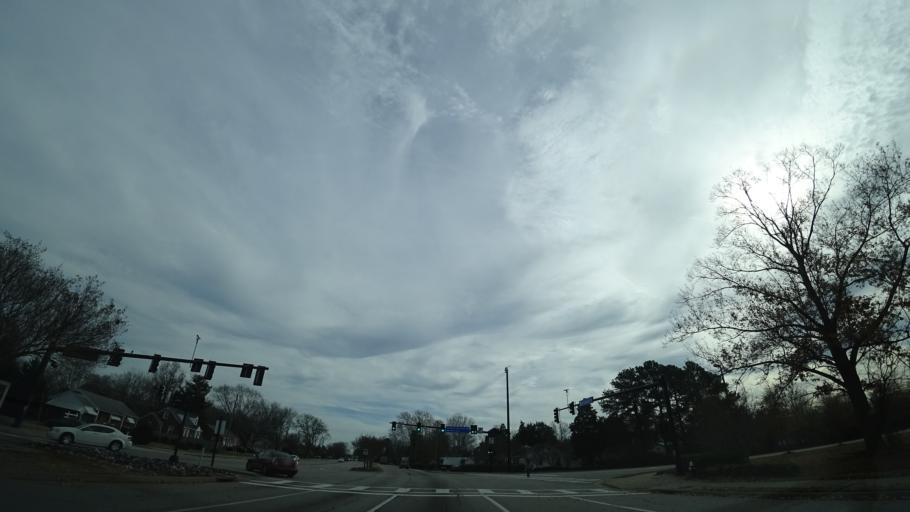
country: US
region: Virginia
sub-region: City of Hampton
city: Hampton
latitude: 37.0405
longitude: -76.3754
